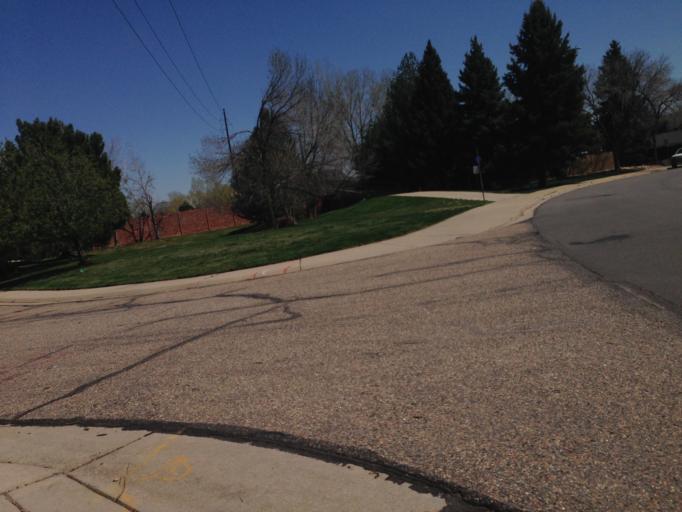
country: US
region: Colorado
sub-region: Boulder County
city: Lafayette
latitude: 39.9906
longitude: -105.1010
